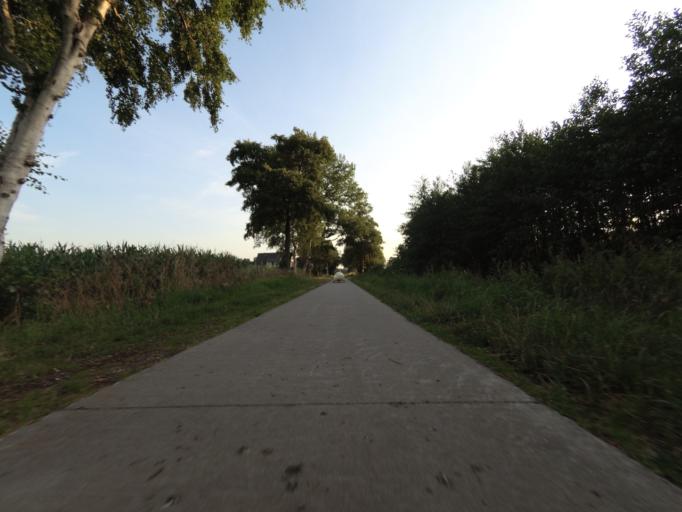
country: NL
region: Overijssel
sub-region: Gemeente Hof van Twente
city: Markelo
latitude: 52.3213
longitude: 6.4937
